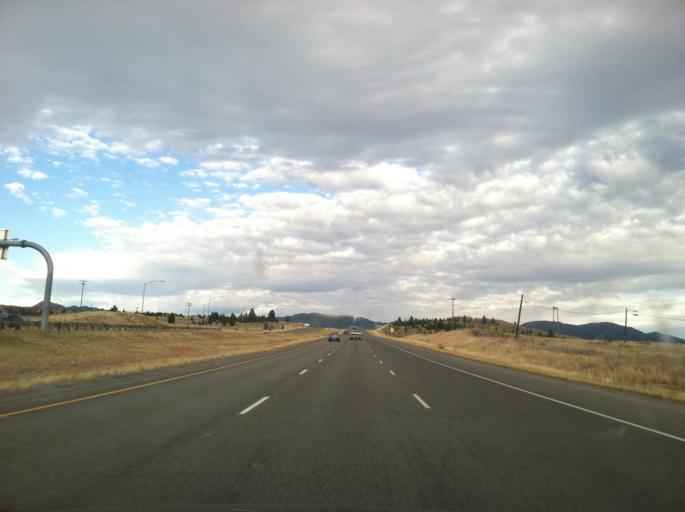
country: US
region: Montana
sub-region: Silver Bow County
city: Butte
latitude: 46.0063
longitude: -112.6062
